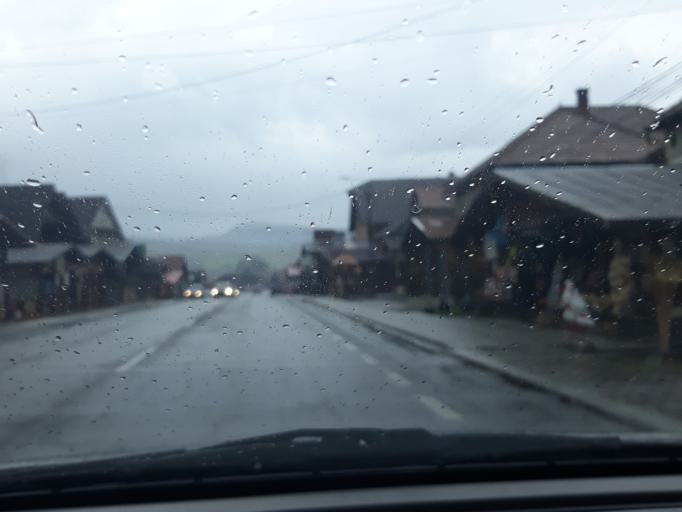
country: RO
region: Harghita
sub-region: Comuna Corund
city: Corund
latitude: 46.4733
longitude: 25.1810
